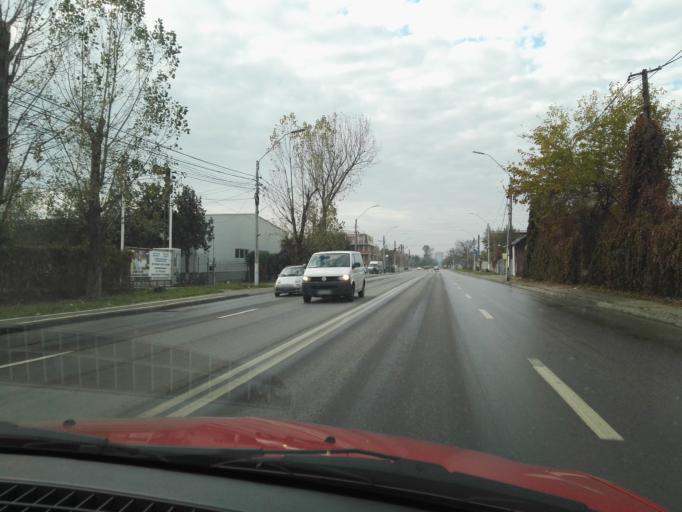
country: RO
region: Ilfov
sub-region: Comuna Magurele
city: Magurele
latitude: 44.3641
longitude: 26.0394
